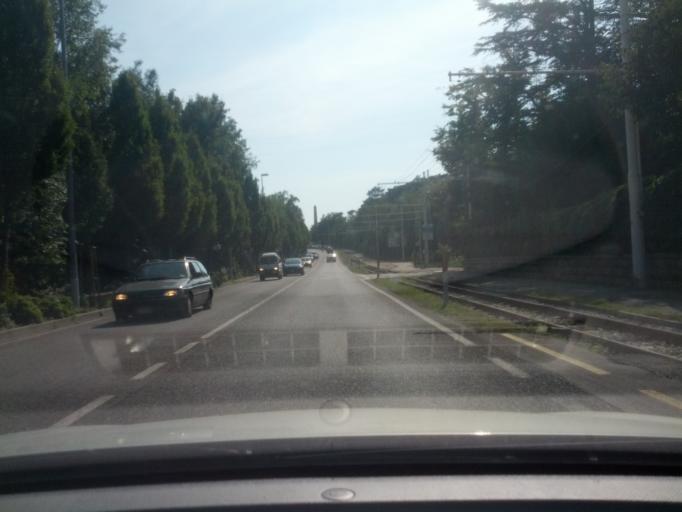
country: IT
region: Friuli Venezia Giulia
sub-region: Provincia di Trieste
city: Villa Opicina
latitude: 45.6825
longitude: 13.7829
